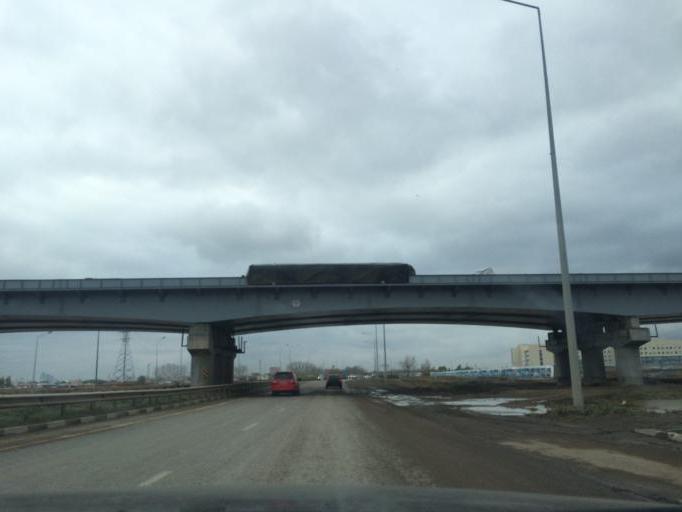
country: KZ
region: Astana Qalasy
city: Astana
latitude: 51.1368
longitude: 71.5341
